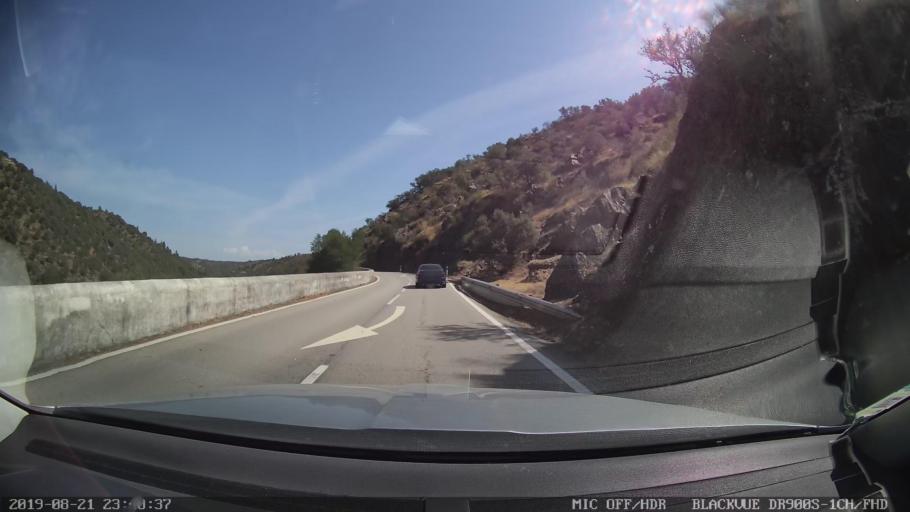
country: PT
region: Castelo Branco
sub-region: Idanha-A-Nova
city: Idanha-a-Nova
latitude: 39.8615
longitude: -7.3301
